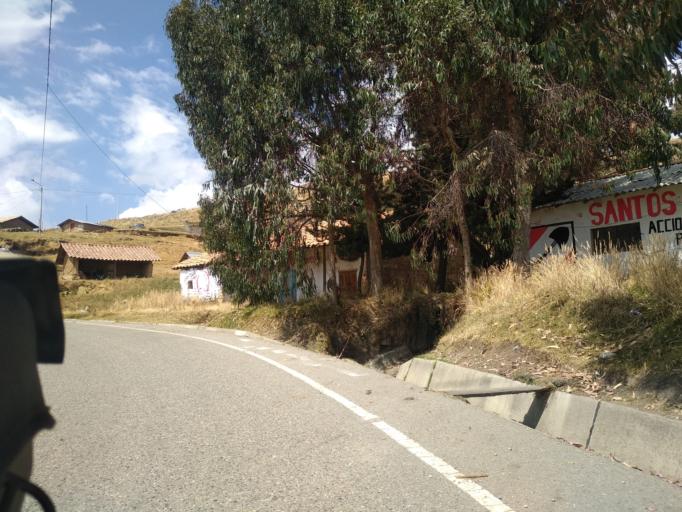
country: PE
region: La Libertad
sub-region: Provincia de Santiago de Chuco
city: Quiruvilca
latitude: -7.9165
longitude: -78.1528
